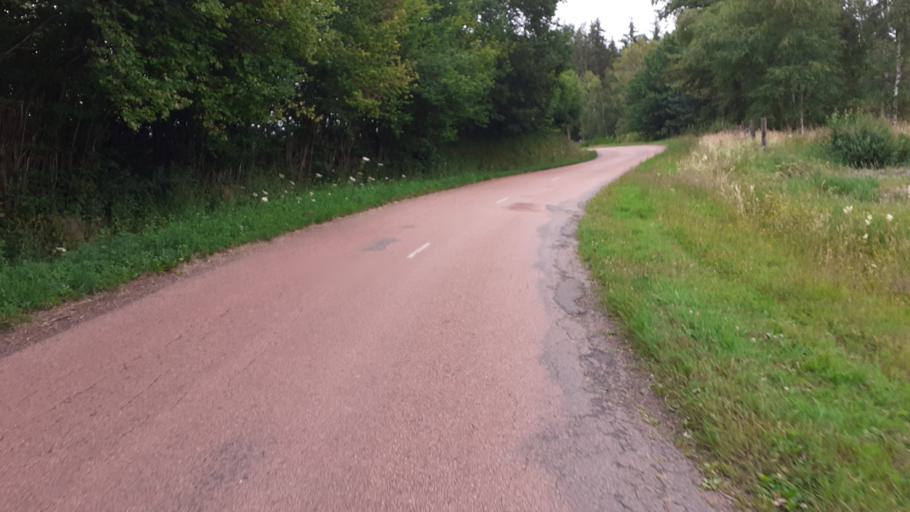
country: FR
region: Bourgogne
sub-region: Departement de la Cote-d'Or
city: Saulieu
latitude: 47.2795
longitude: 4.1417
